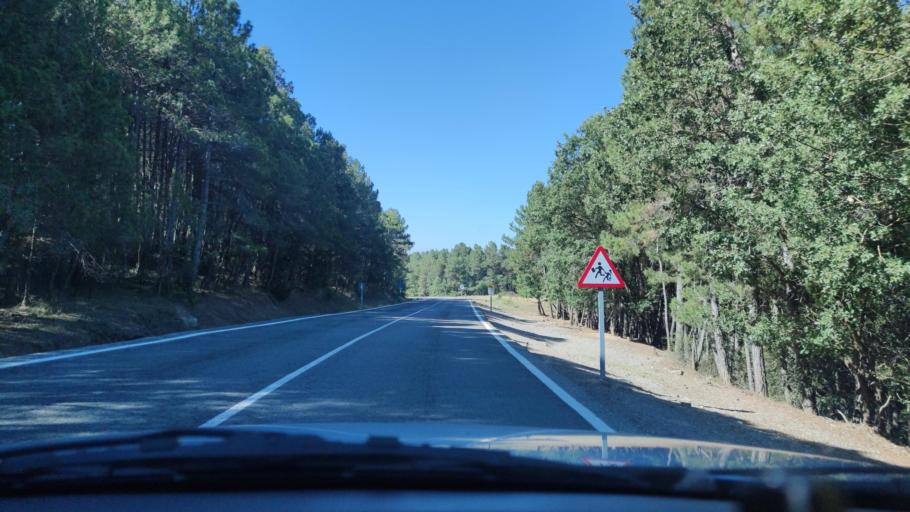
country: ES
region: Catalonia
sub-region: Provincia de Lleida
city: Solsona
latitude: 41.9036
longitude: 1.5360
